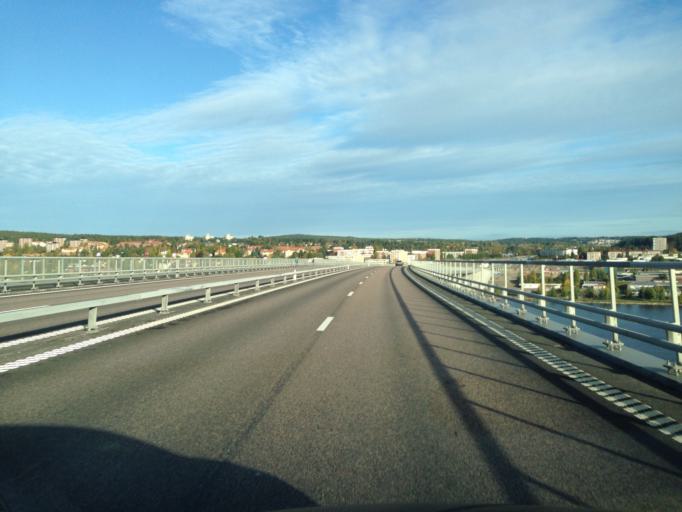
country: SE
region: Vaesternorrland
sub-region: Sundsvalls Kommun
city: Sundsvall
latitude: 62.3890
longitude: 17.3411
